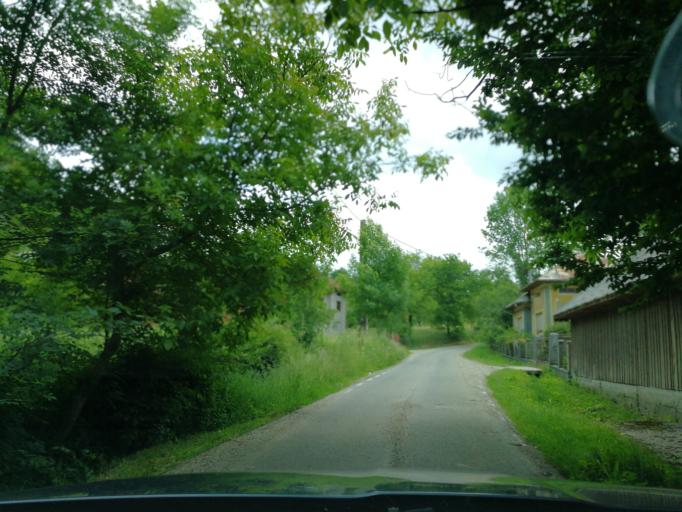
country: RO
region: Maramures
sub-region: Comuna Sisesti
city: Sisesti
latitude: 47.6164
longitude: 23.7167
